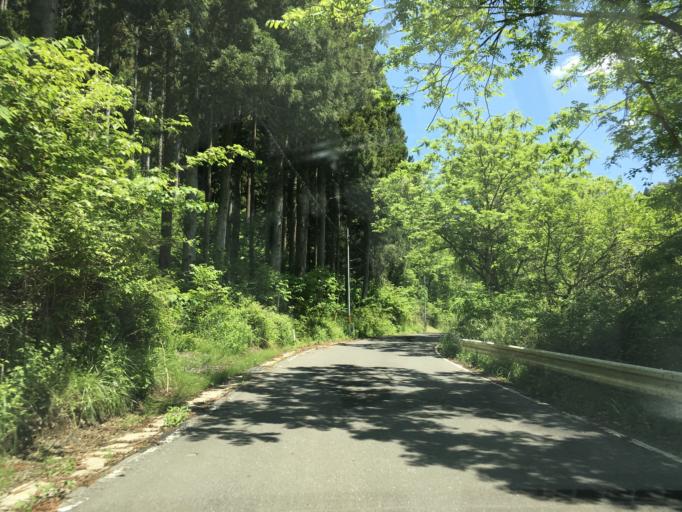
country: JP
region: Miyagi
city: Wakuya
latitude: 38.6694
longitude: 141.3396
